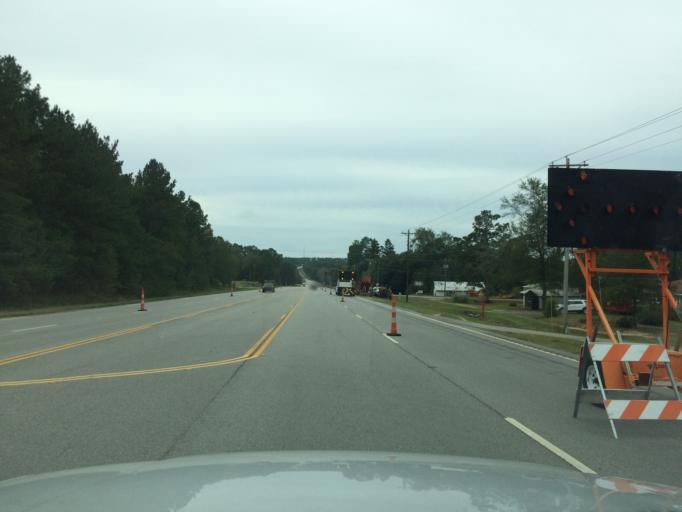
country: US
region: South Carolina
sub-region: Aiken County
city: Aiken
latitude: 33.6155
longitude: -81.6805
